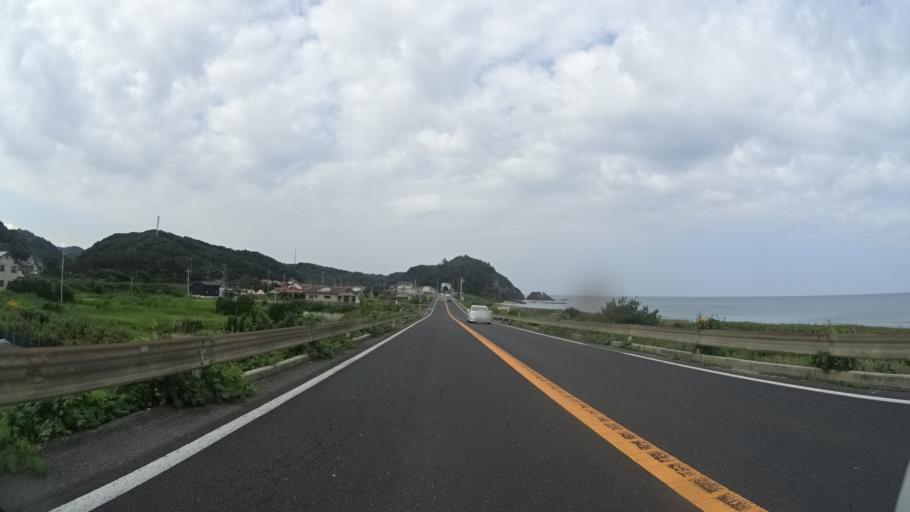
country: JP
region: Shimane
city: Odacho-oda
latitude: 35.1959
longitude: 132.4462
